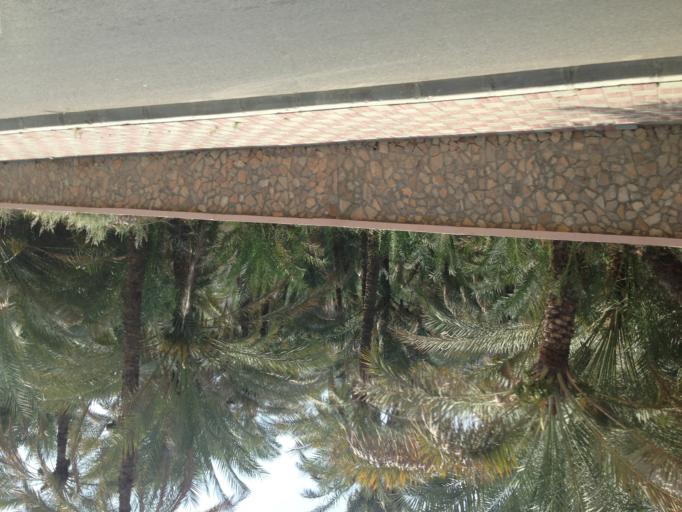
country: OM
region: Ash Sharqiyah
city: Ibra'
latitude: 23.0855
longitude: 58.8664
